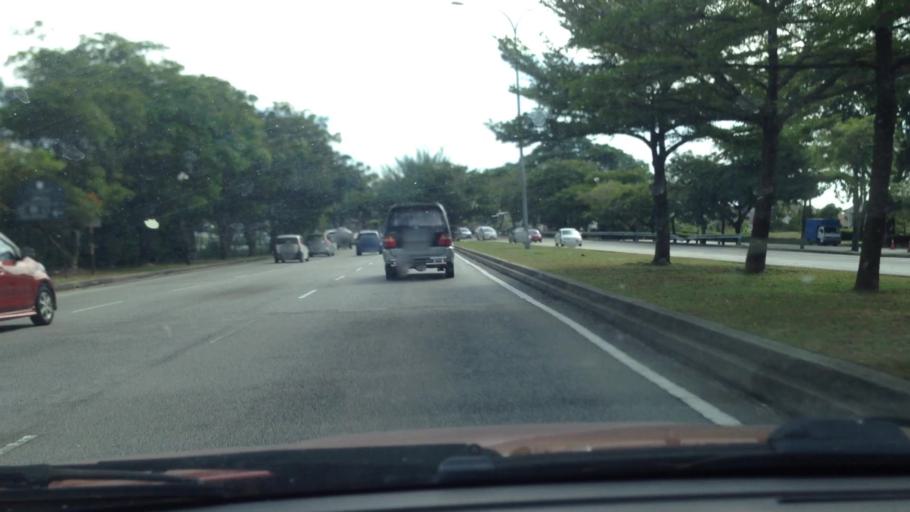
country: MY
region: Selangor
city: Subang Jaya
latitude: 3.0595
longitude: 101.5796
